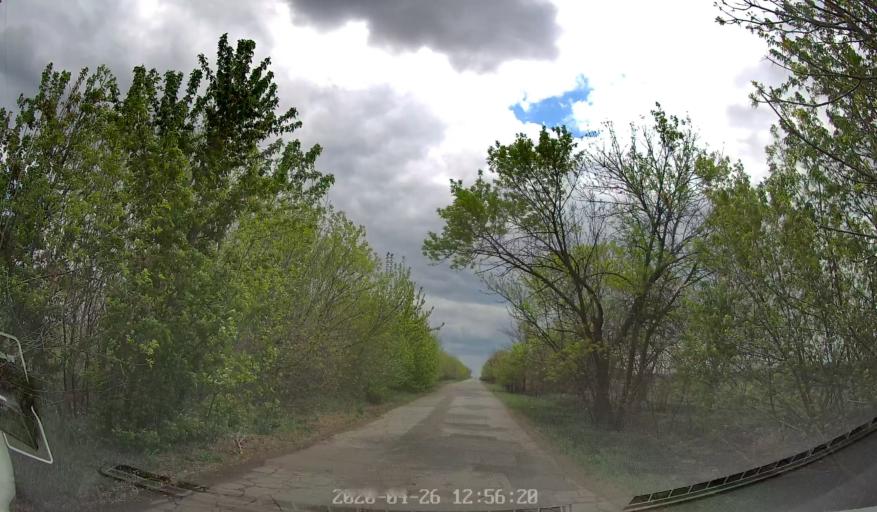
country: MD
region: Chisinau
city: Vadul lui Voda
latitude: 47.0735
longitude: 29.0660
